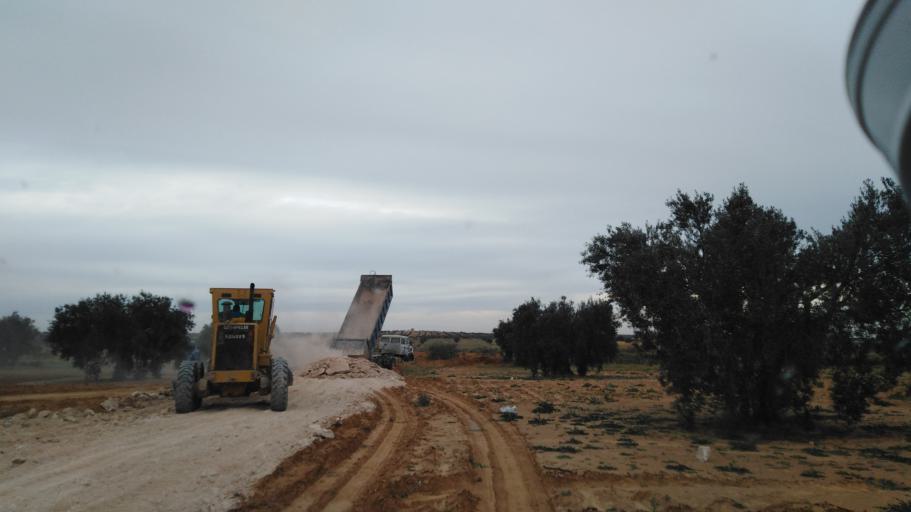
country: TN
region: Safaqis
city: Bi'r `Ali Bin Khalifah
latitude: 34.7699
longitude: 10.3742
